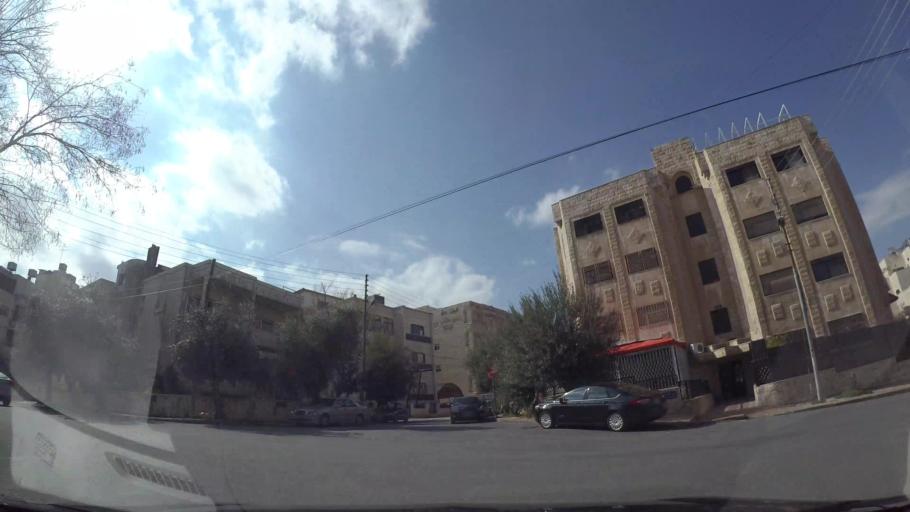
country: JO
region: Amman
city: Al Jubayhah
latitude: 31.9770
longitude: 35.8906
